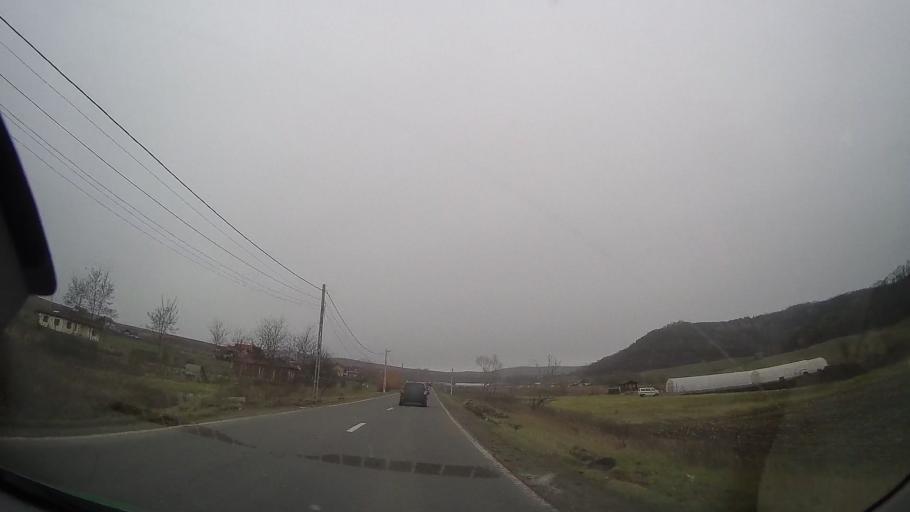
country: RO
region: Mures
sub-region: Comuna Ceausu de Campie
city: Ceausu de Campie
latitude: 46.6285
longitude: 24.5201
